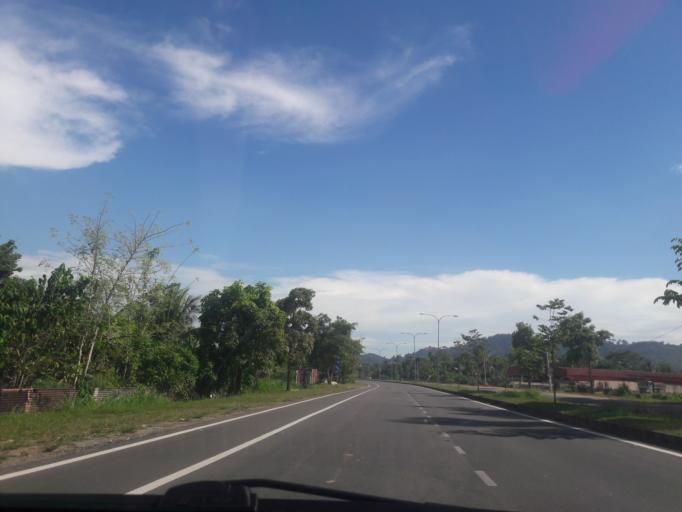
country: MY
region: Kedah
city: Sungai Petani
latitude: 5.6260
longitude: 100.4639
